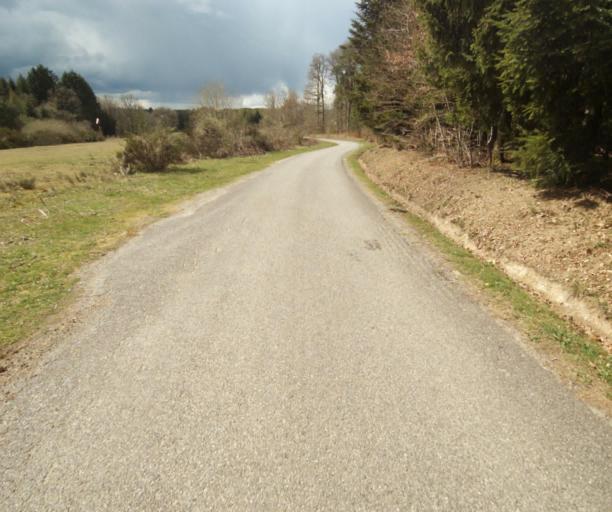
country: FR
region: Limousin
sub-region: Departement de la Correze
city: Correze
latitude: 45.2718
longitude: 1.9763
